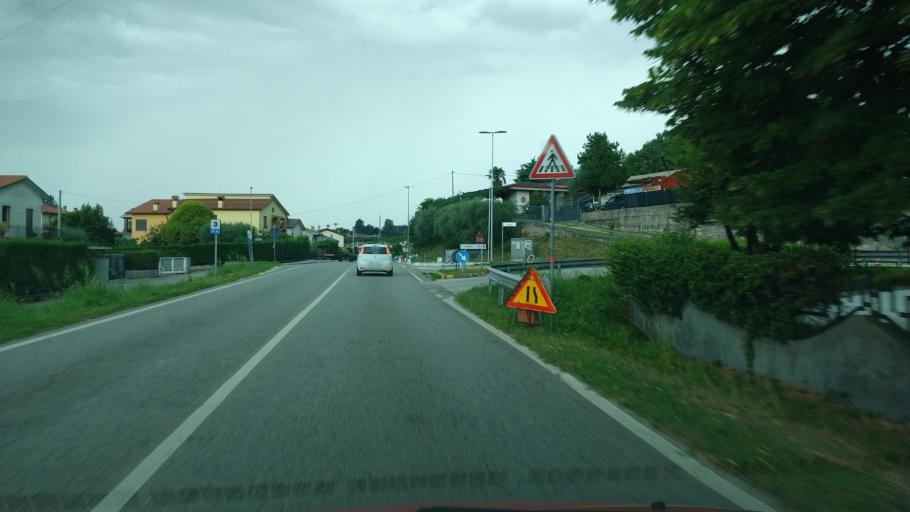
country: IT
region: Veneto
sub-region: Provincia di Vicenza
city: Zugliano
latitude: 45.7302
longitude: 11.5154
